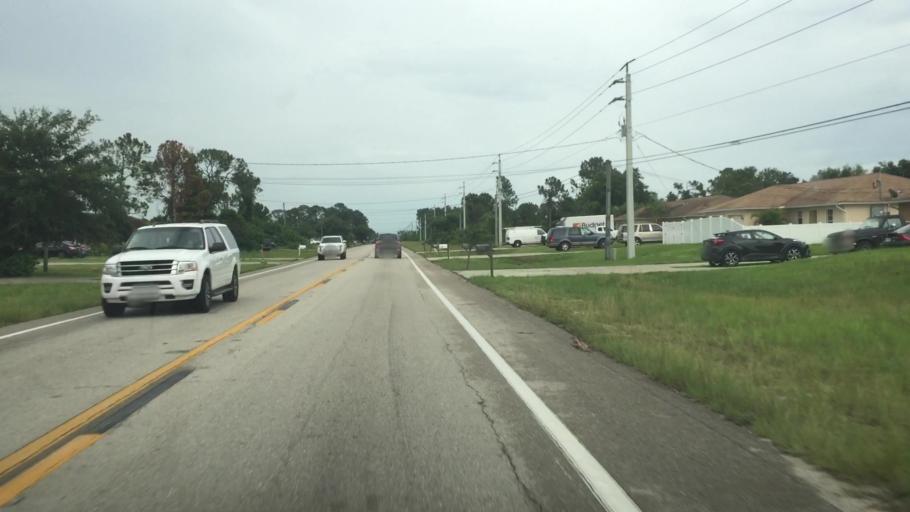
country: US
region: Florida
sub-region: Lee County
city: Gateway
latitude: 26.5976
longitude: -81.7305
